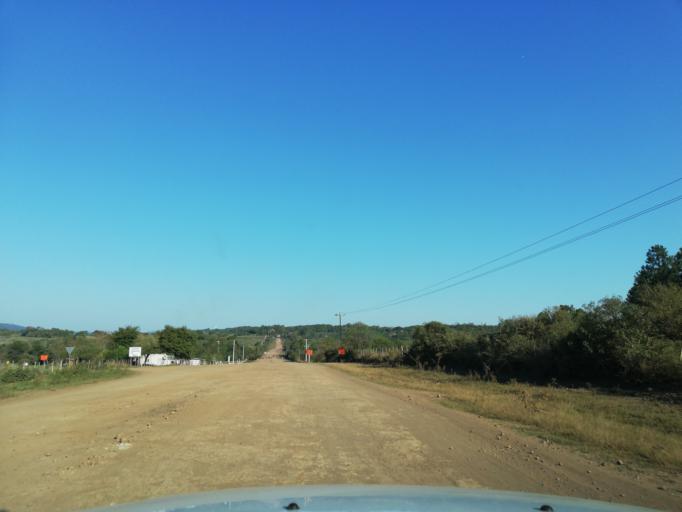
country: AR
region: Misiones
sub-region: Departamento de Candelaria
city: Candelaria
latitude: -27.5317
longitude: -55.7191
